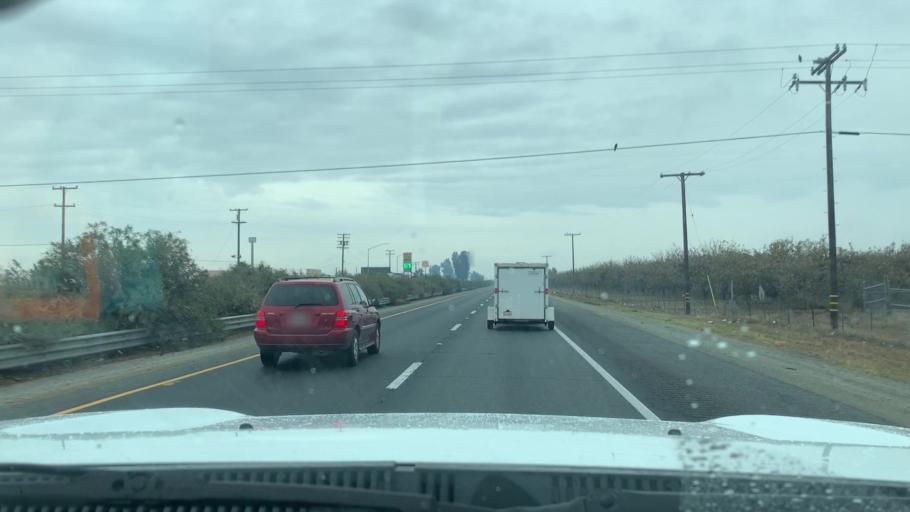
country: US
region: California
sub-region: Kern County
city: Delano
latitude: 35.8191
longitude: -119.2584
